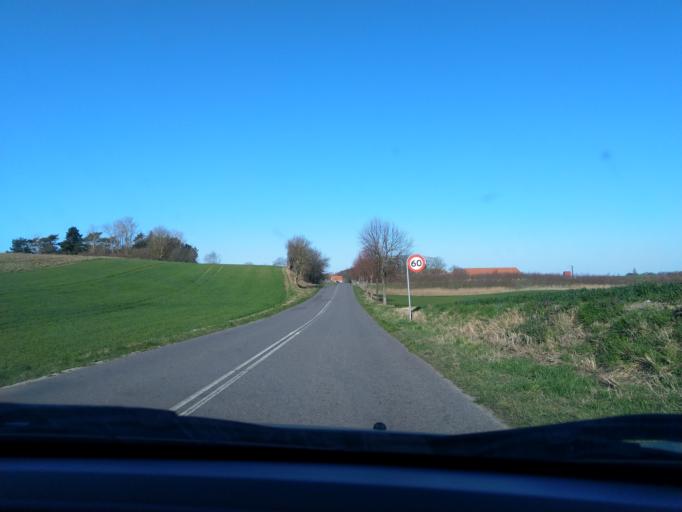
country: DK
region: Zealand
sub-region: Kalundborg Kommune
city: Kalundborg
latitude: 55.7306
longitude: 10.9846
